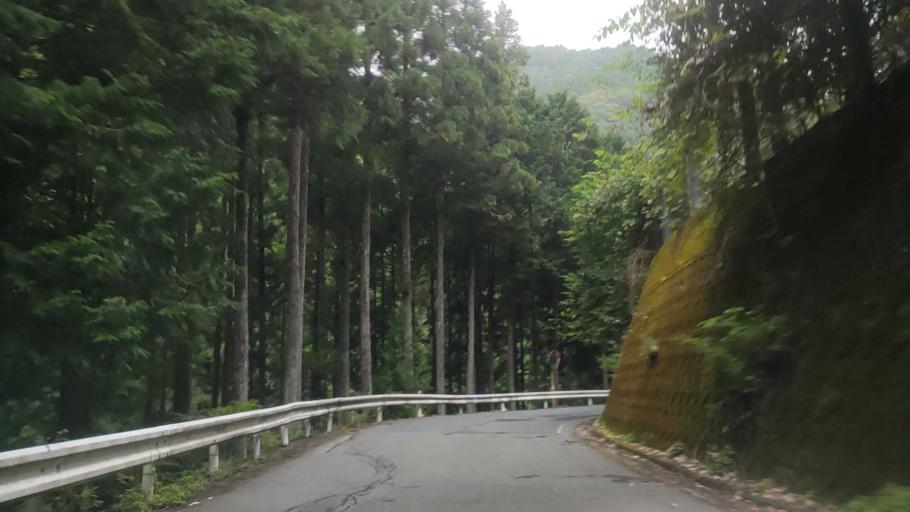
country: JP
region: Wakayama
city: Koya
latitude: 34.2365
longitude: 135.6490
